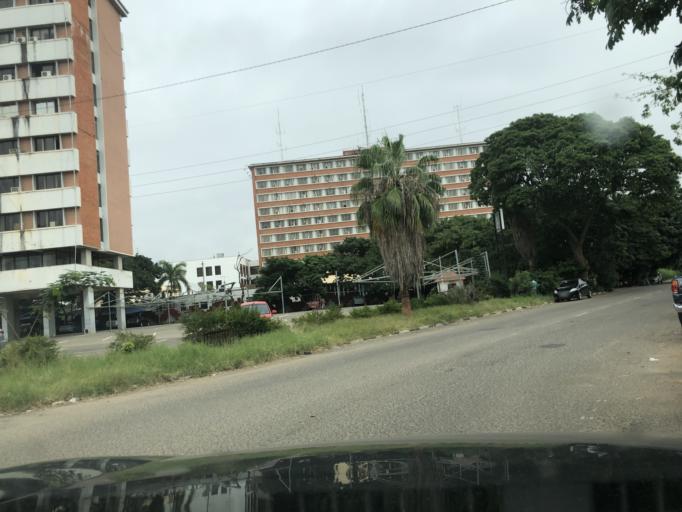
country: AO
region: Luanda
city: Luanda
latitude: -8.8282
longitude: 13.2414
